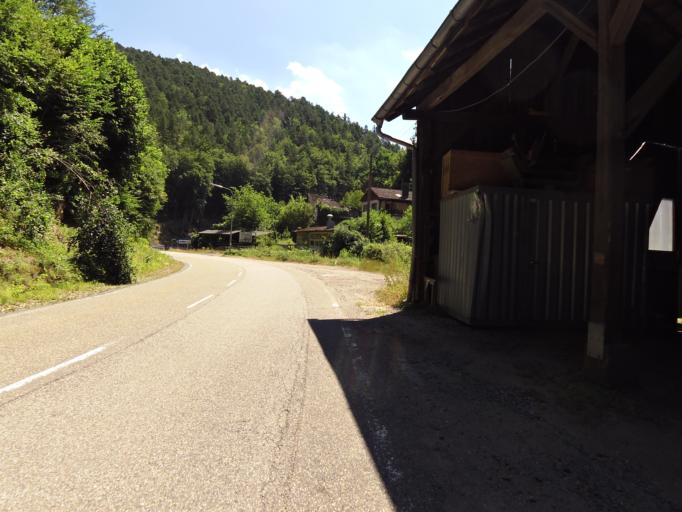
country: DE
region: Rheinland-Pfalz
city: Elmstein
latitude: 49.3569
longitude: 7.9274
